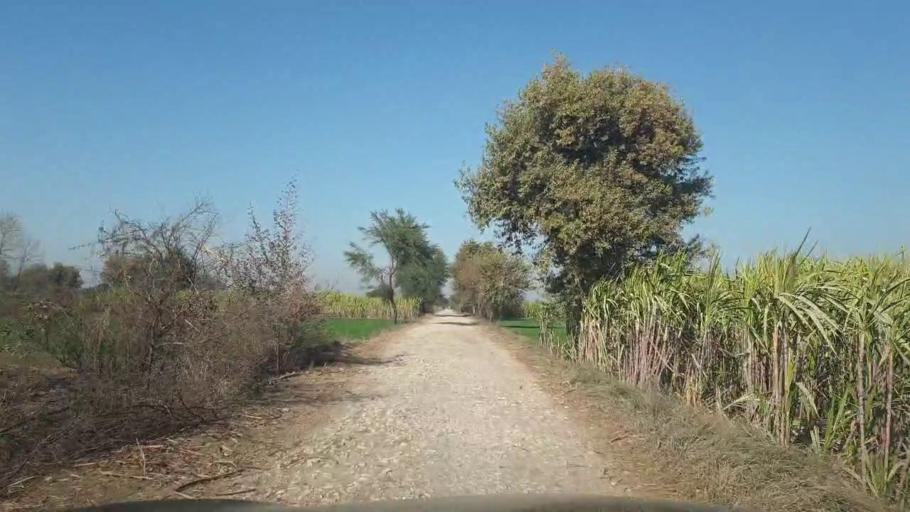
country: PK
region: Sindh
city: Mirpur Mathelo
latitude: 27.9978
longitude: 69.4795
